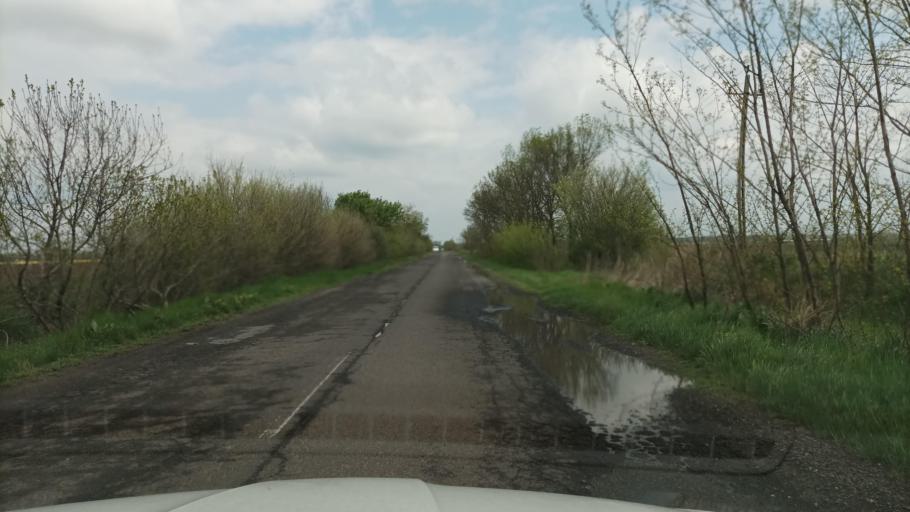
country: HU
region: Pest
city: Nagykoros
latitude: 47.0364
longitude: 19.8247
